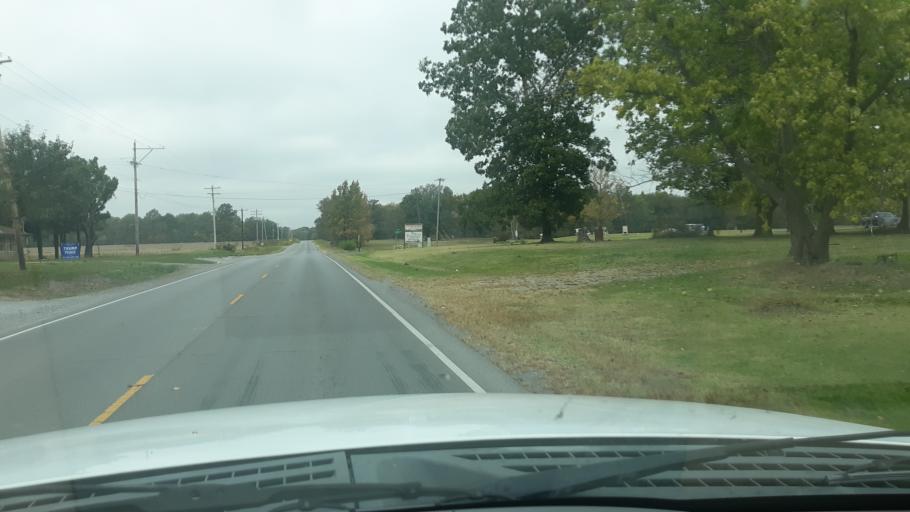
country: US
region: Illinois
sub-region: Saline County
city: Eldorado
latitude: 37.8207
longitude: -88.4836
